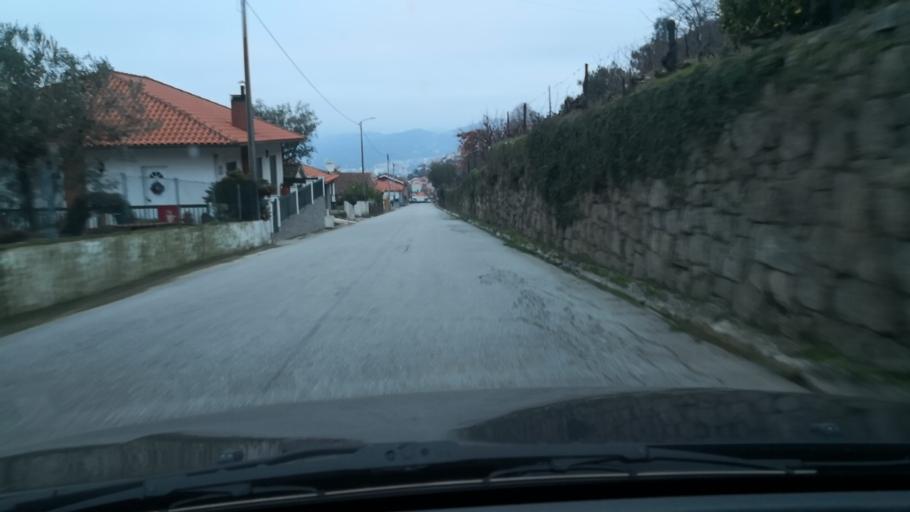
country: PT
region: Viseu
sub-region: Lamego
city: Lamego
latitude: 41.1225
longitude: -7.8028
